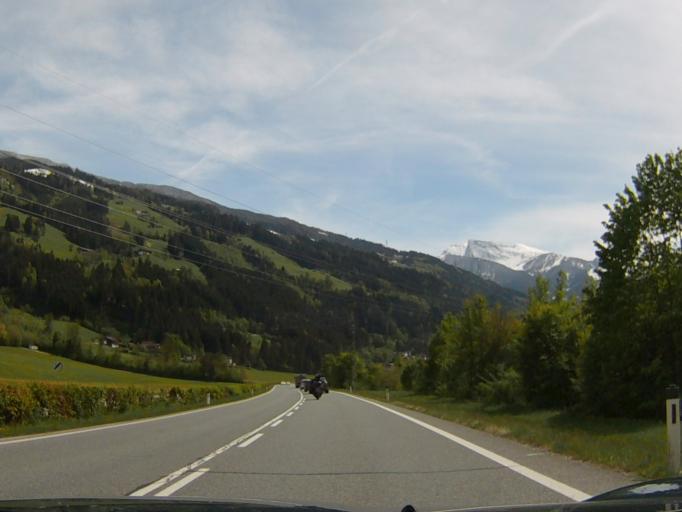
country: AT
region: Tyrol
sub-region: Politischer Bezirk Schwaz
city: Stumm
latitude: 47.2597
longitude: 11.8994
